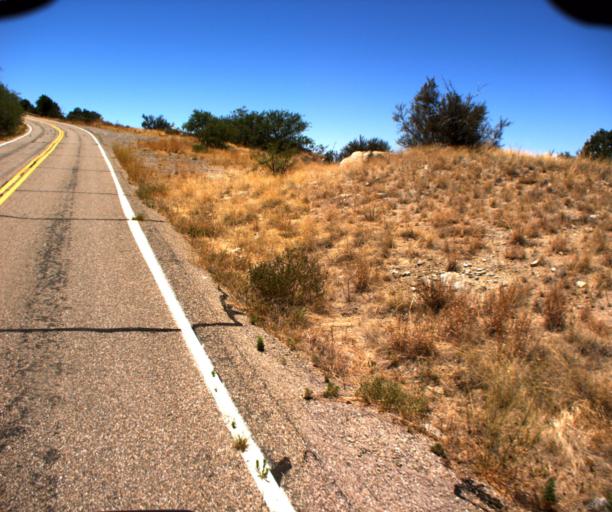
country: US
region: Arizona
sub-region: Pima County
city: Sells
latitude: 31.9633
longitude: -111.6218
